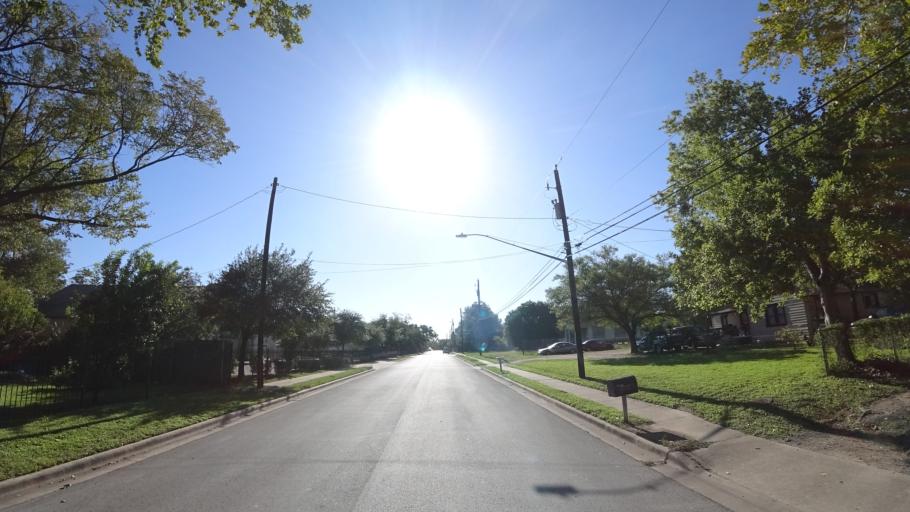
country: US
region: Texas
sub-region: Travis County
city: Austin
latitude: 30.3535
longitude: -97.7026
